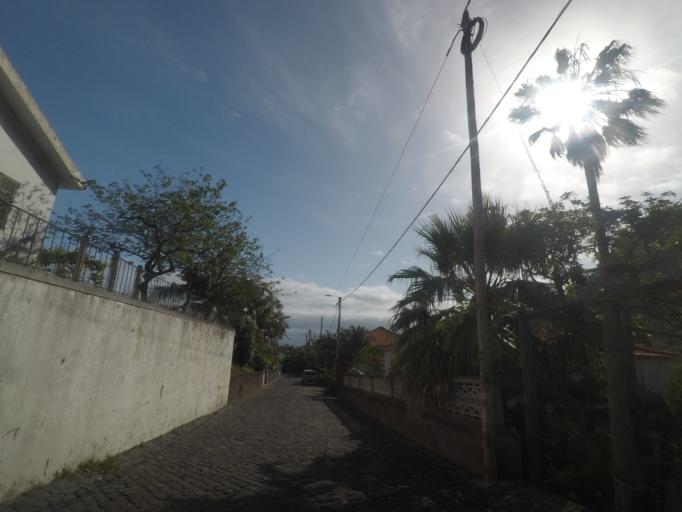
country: PT
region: Madeira
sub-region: Sao Vicente
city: Sao Vicente
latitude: 32.8263
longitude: -16.9872
